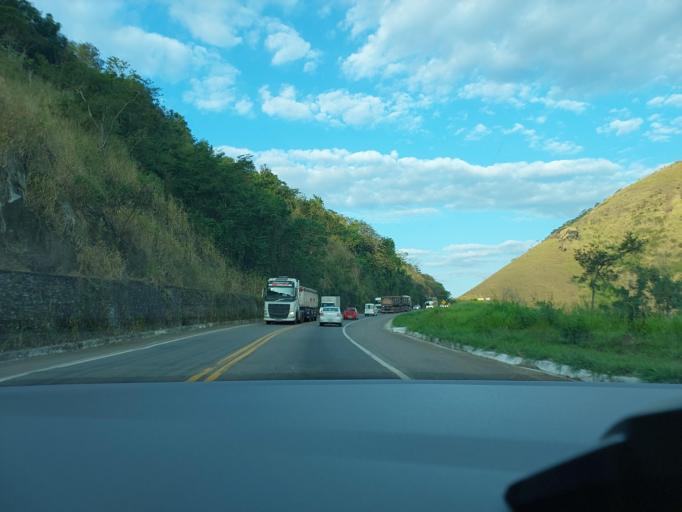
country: BR
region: Minas Gerais
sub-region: Muriae
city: Muriae
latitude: -21.1251
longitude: -42.2536
